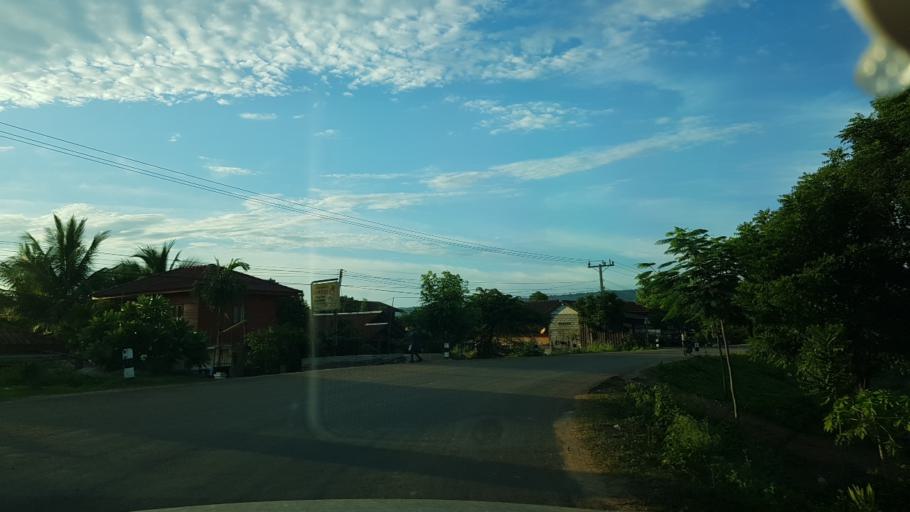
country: TH
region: Nong Khai
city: Sangkhom
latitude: 18.0938
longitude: 102.2866
